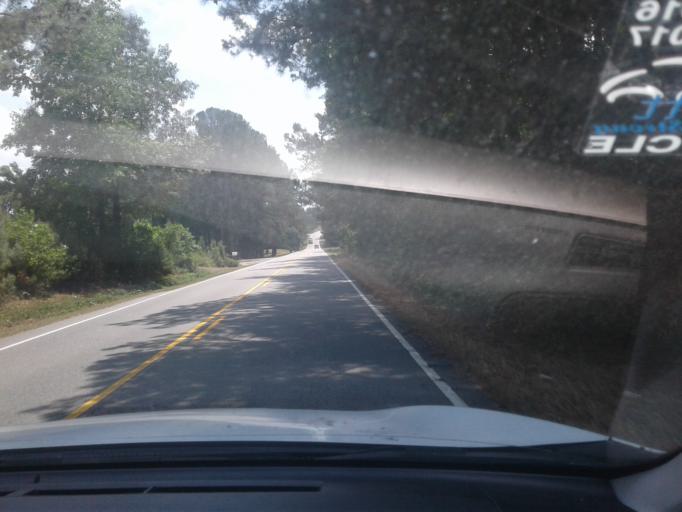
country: US
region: North Carolina
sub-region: Johnston County
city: Benson
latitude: 35.4100
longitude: -78.5404
